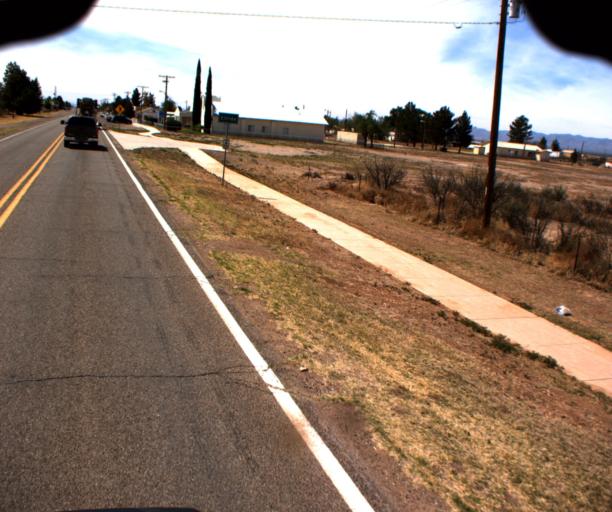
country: US
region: Arizona
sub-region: Cochise County
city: Bisbee
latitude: 31.6884
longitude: -109.6874
